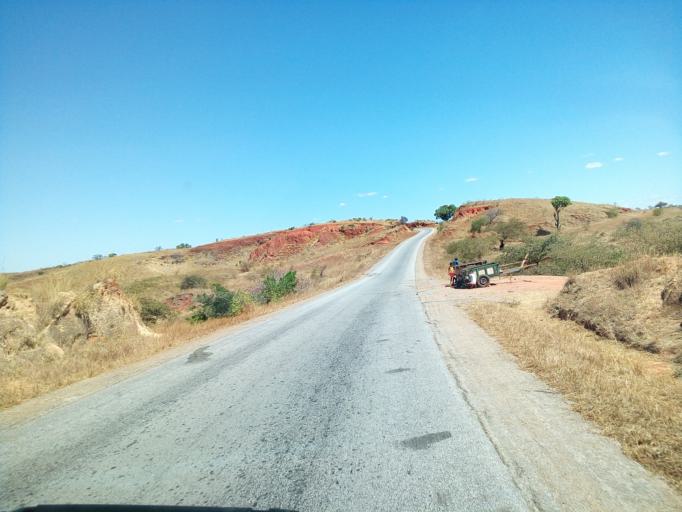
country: MG
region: Betsiboka
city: Maevatanana
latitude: -17.1297
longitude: 46.8096
